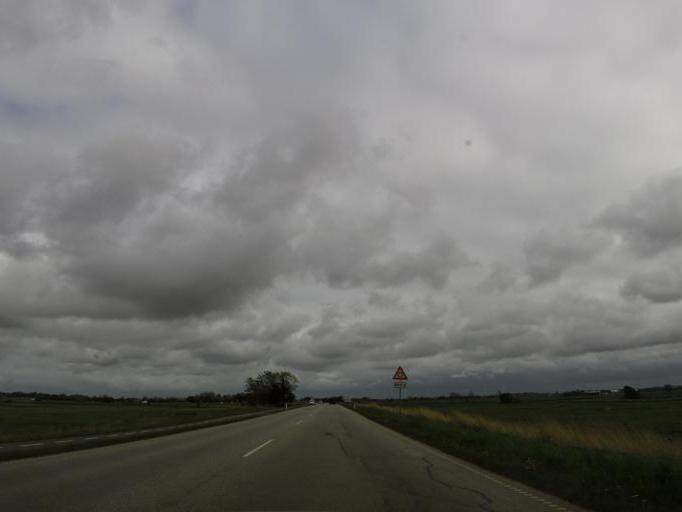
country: DK
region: South Denmark
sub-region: Tonder Kommune
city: Tonder
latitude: 54.9318
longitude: 8.8852
